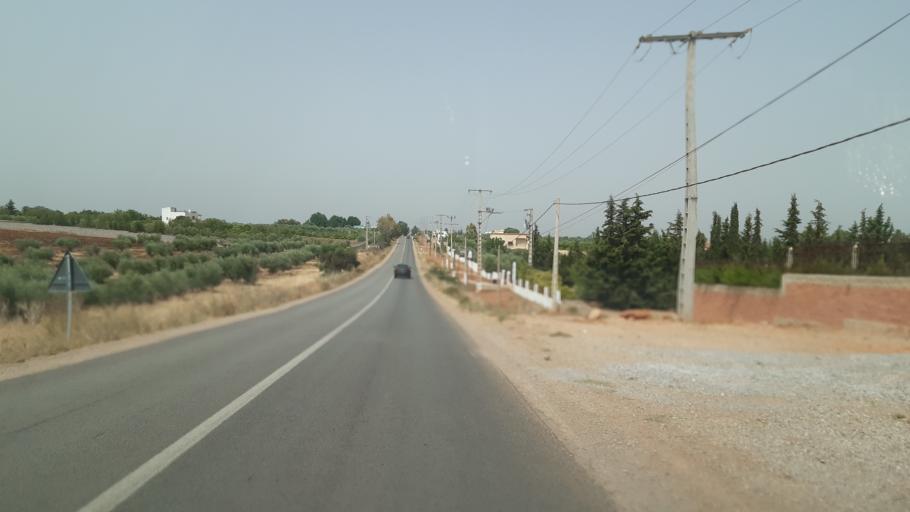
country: MA
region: Fes-Boulemane
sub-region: Fes
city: Oulad Tayeb
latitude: 33.8948
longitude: -5.0237
